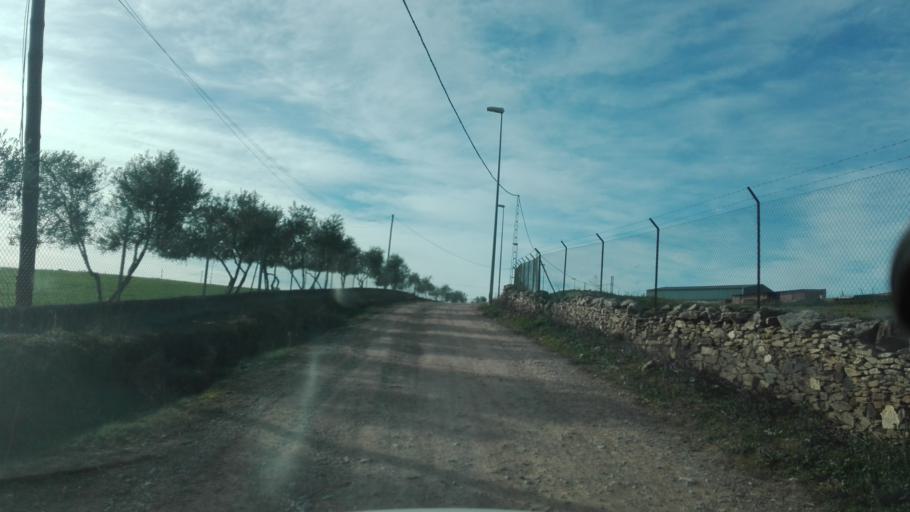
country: ES
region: Extremadura
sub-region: Provincia de Badajoz
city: Usagre
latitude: 38.3588
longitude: -6.1581
